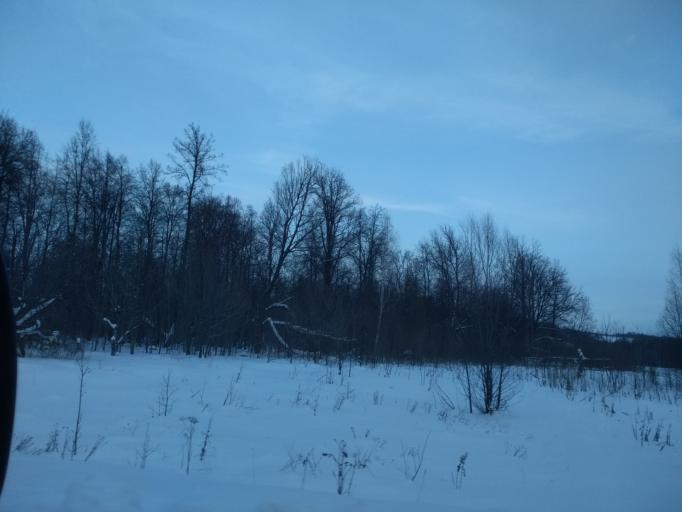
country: RU
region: Bashkortostan
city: Kudeyevskiy
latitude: 54.7174
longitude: 56.6065
